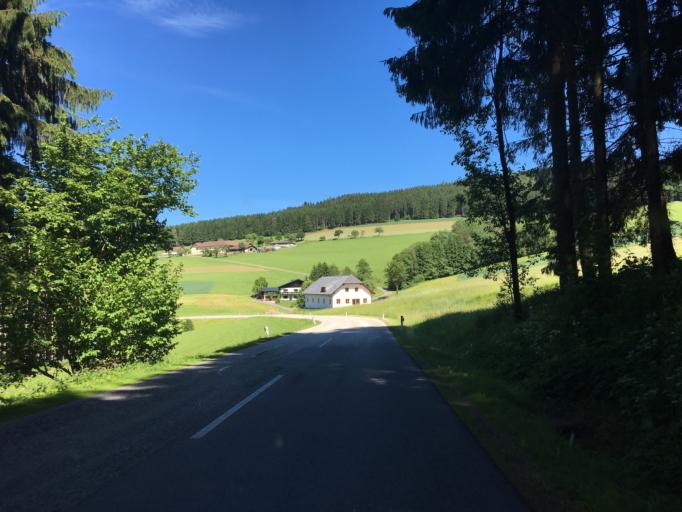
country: AT
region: Upper Austria
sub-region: Politischer Bezirk Urfahr-Umgebung
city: Zwettl an der Rodl
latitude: 48.4450
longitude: 14.2574
